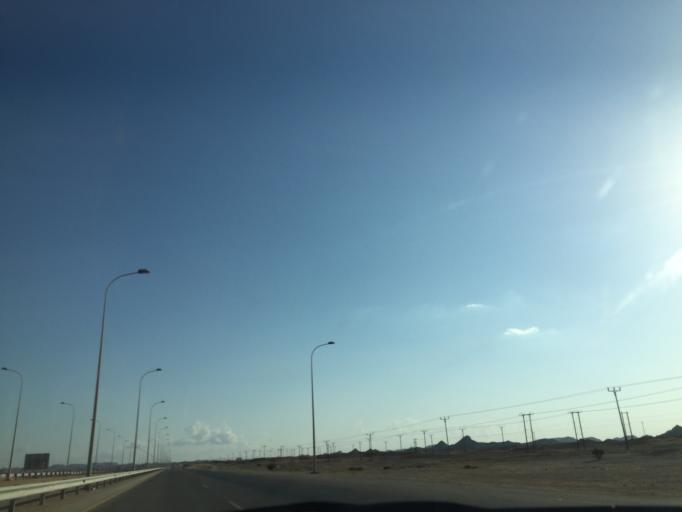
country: OM
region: Zufar
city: Salalah
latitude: 17.5289
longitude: 54.0557
